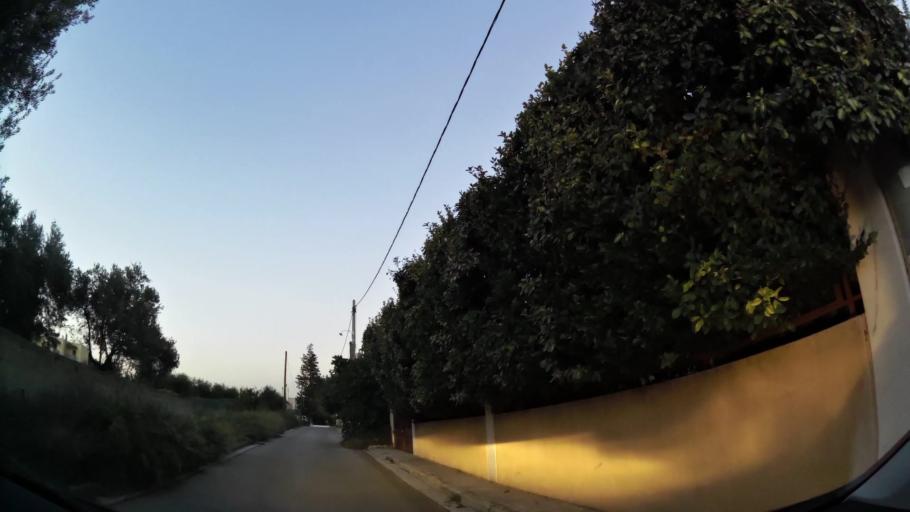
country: GR
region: Attica
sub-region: Nomarchia Anatolikis Attikis
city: Paiania
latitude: 37.9476
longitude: 23.8585
